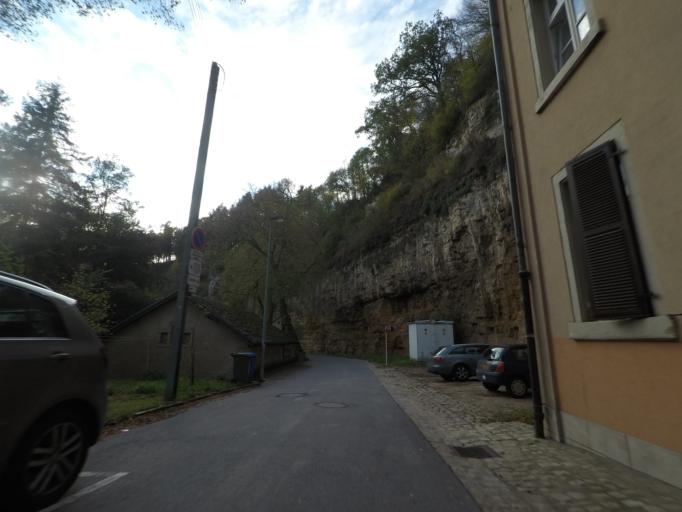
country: LU
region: Luxembourg
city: Kirchberg
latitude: 49.6085
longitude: 6.1629
